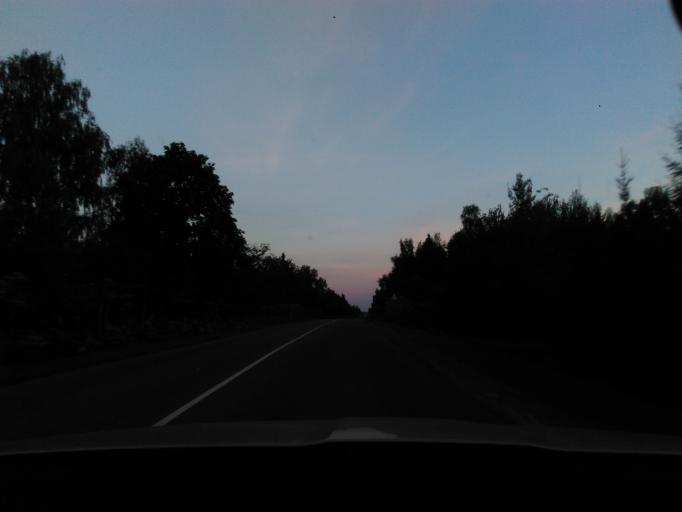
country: RU
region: Moskovskaya
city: Klin
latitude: 56.2443
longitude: 36.7571
